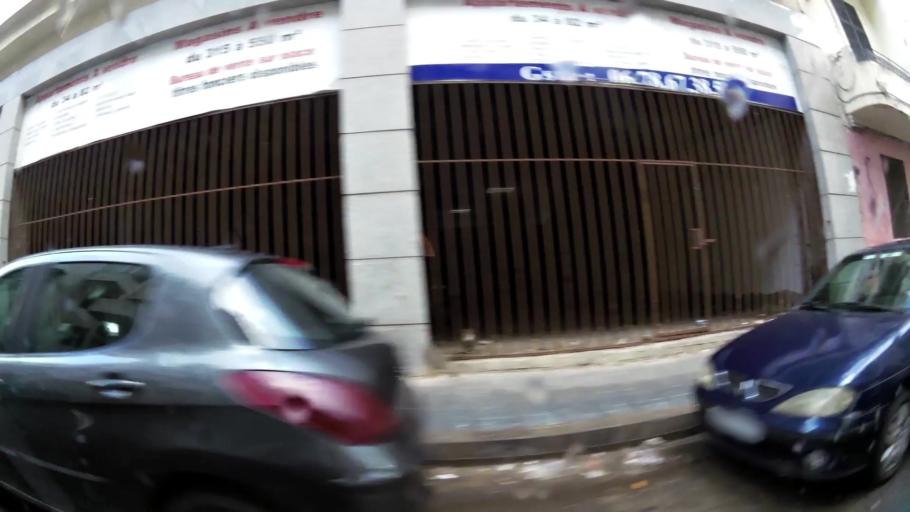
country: MA
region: Grand Casablanca
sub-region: Casablanca
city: Casablanca
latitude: 33.5897
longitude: -7.6160
